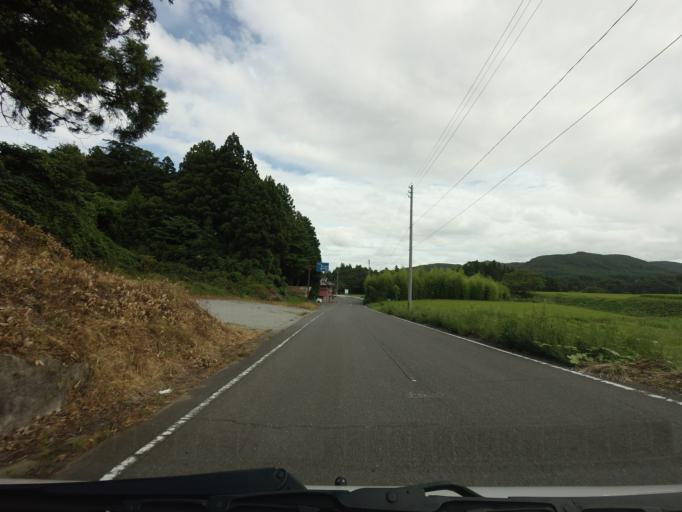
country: JP
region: Fukushima
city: Motomiya
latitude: 37.5399
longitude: 140.3346
